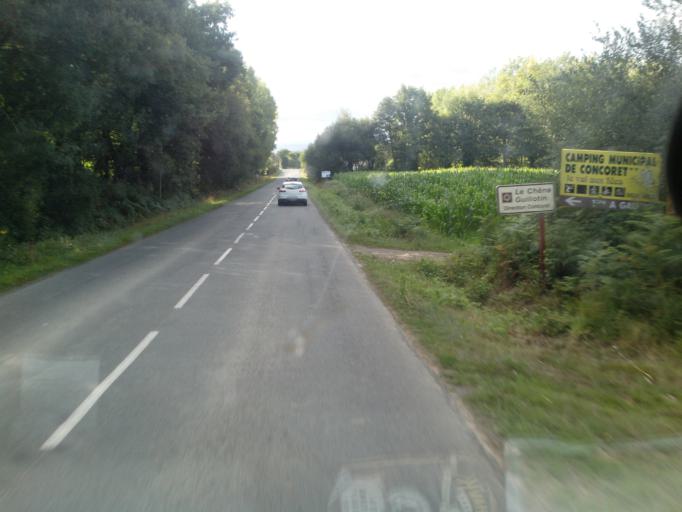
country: FR
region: Brittany
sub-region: Departement d'Ille-et-Vilaine
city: Paimpont
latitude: 48.0637
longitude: -2.1862
